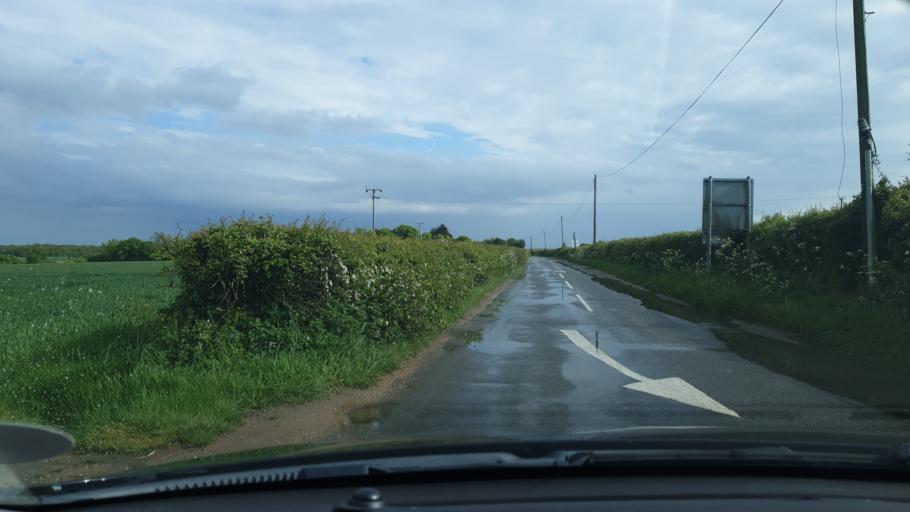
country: GB
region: England
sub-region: Essex
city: Great Bentley
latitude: 51.8489
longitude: 1.0455
